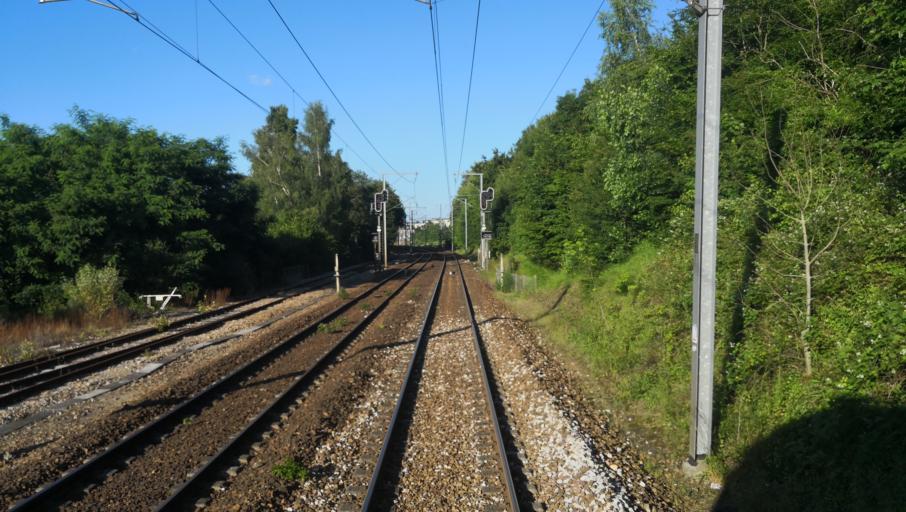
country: FR
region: Haute-Normandie
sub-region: Departement de l'Eure
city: Evreux
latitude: 49.0158
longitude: 1.1363
